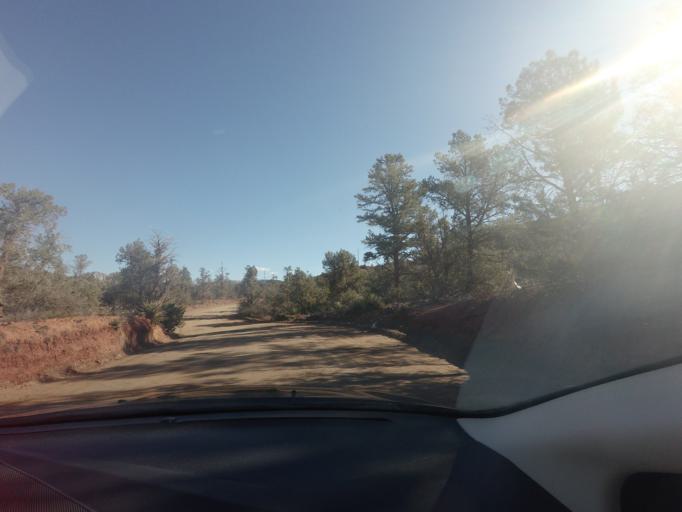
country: US
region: Arizona
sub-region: Yavapai County
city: West Sedona
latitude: 34.8190
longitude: -111.8093
